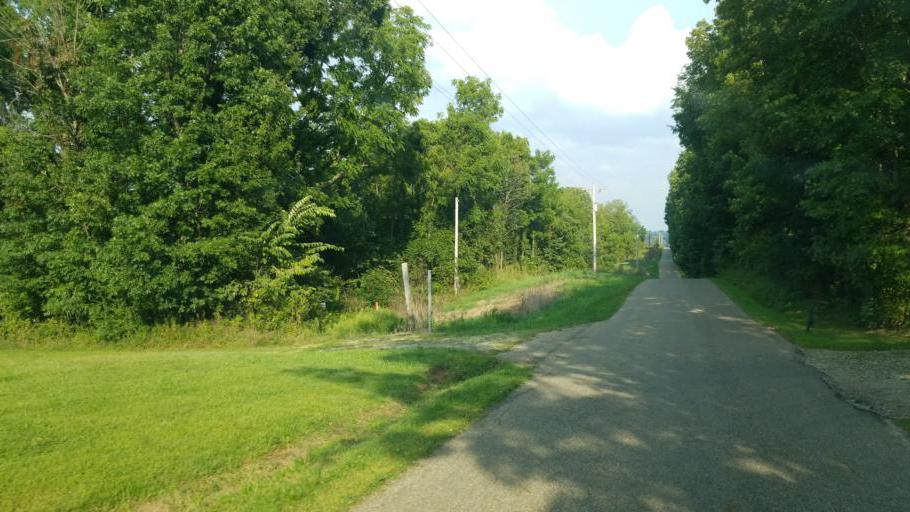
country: US
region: Ohio
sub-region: Knox County
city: Gambier
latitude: 40.3532
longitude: -82.4049
